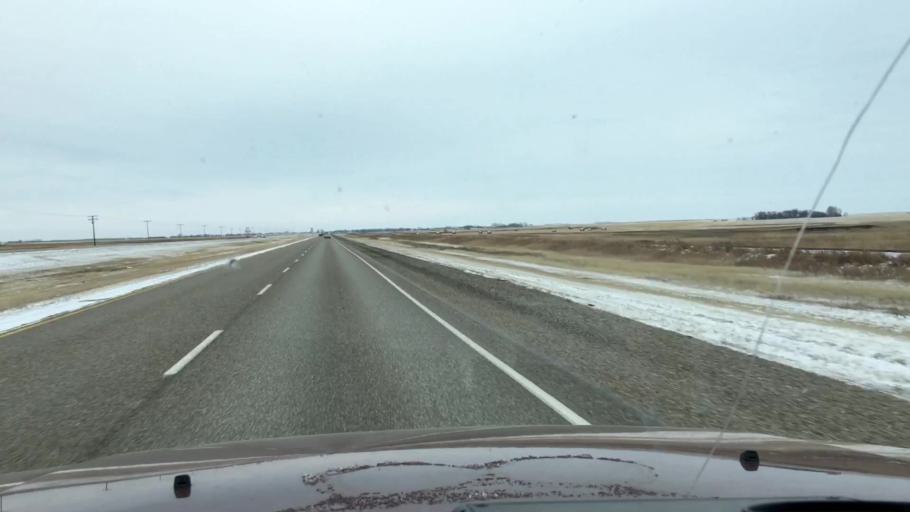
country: CA
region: Saskatchewan
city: Watrous
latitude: 51.0844
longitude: -105.8522
